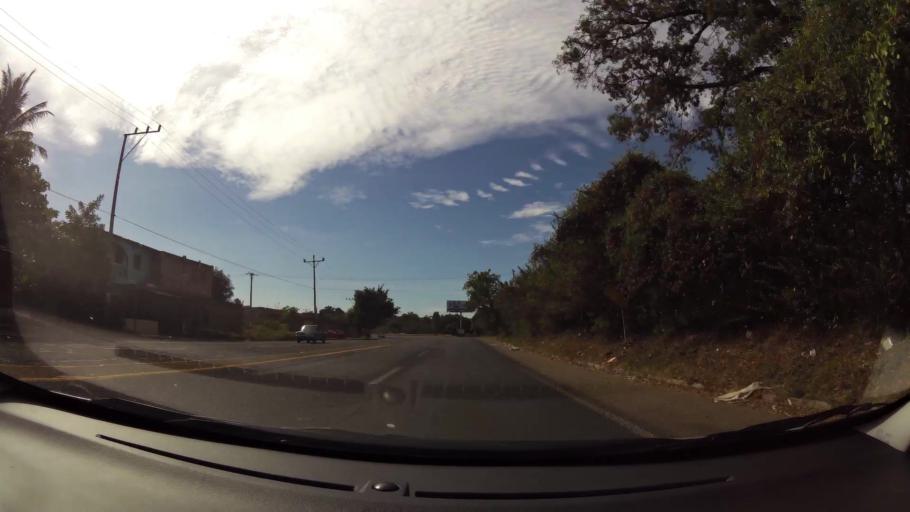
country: SV
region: Santa Ana
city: Chalchuapa
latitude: 13.9883
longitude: -89.6876
